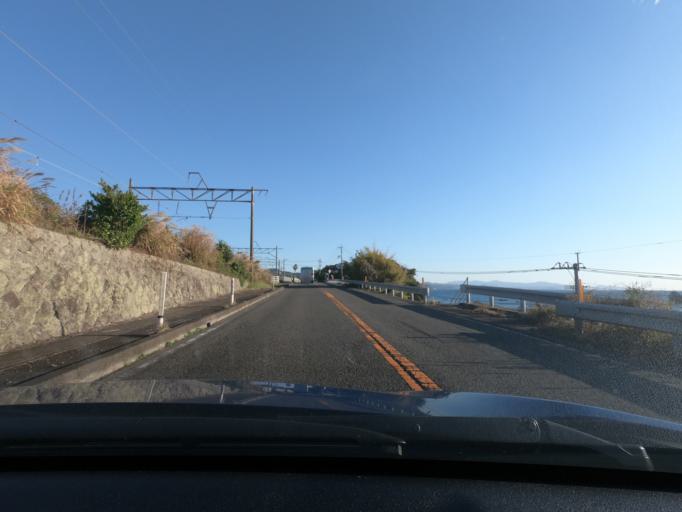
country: JP
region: Kagoshima
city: Akune
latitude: 31.9760
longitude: 130.2049
